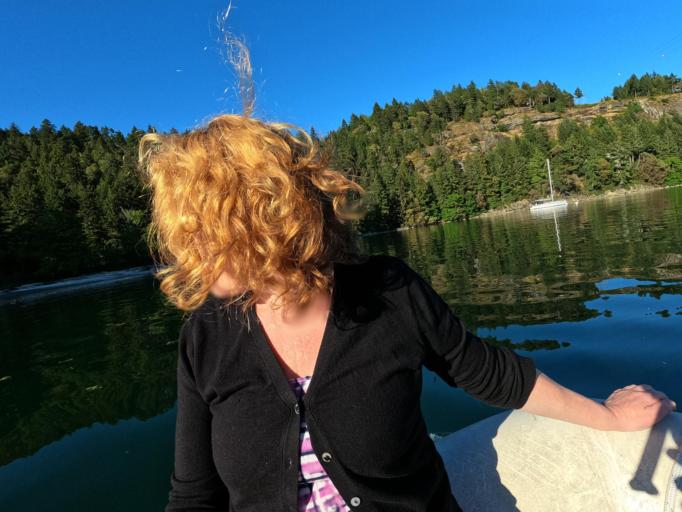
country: CA
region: British Columbia
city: North Saanich
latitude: 48.8970
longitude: -123.4020
